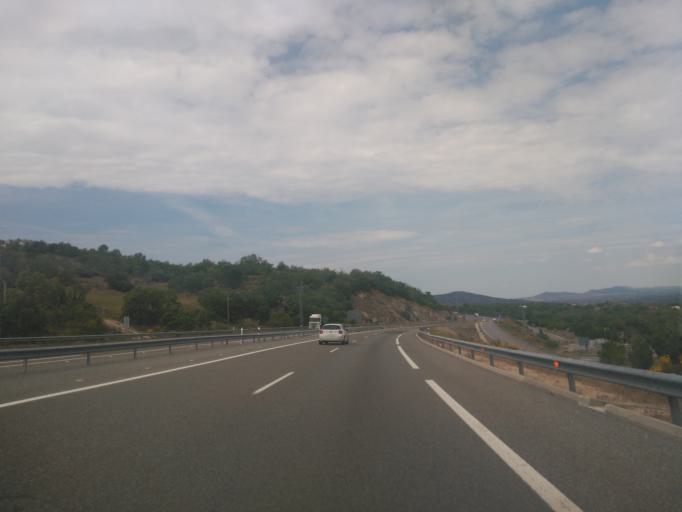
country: ES
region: Castille and Leon
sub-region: Provincia de Salamanca
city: Sorihuela
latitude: 40.4380
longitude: -5.6930
